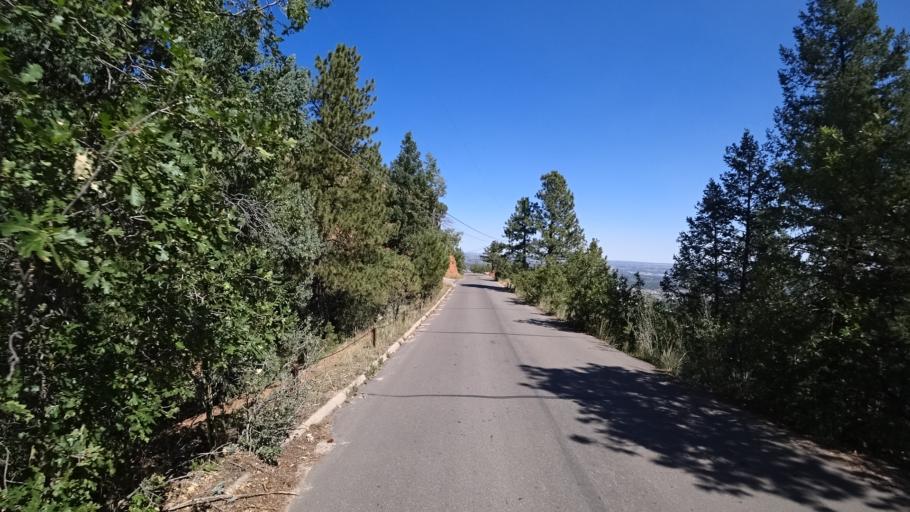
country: US
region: Colorado
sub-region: El Paso County
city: Colorado Springs
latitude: 38.8038
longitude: -104.8774
